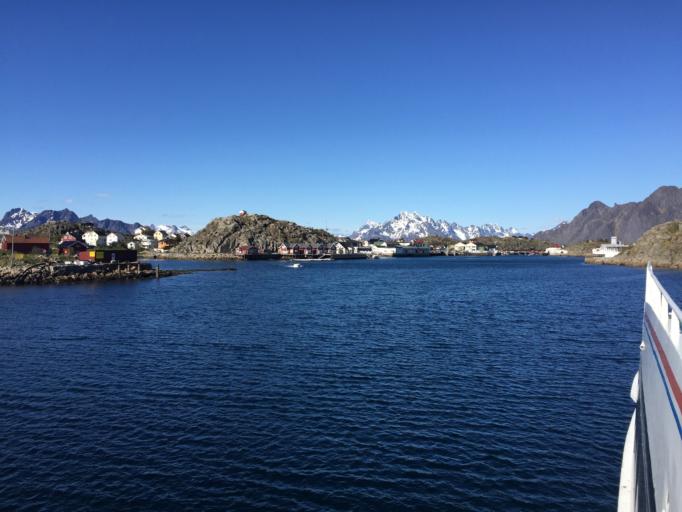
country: NO
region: Nordland
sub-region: Vagan
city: Svolvaer
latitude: 68.1619
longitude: 14.6572
